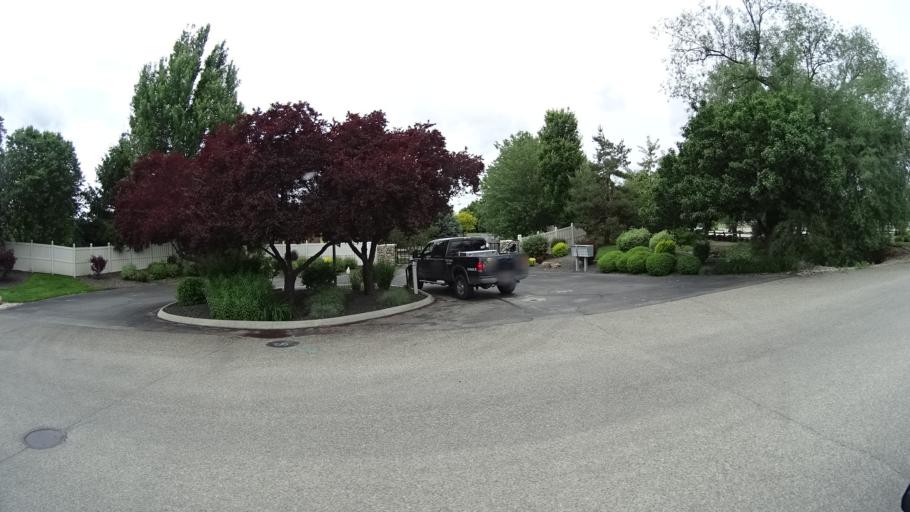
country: US
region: Idaho
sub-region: Ada County
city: Eagle
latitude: 43.6808
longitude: -116.3141
